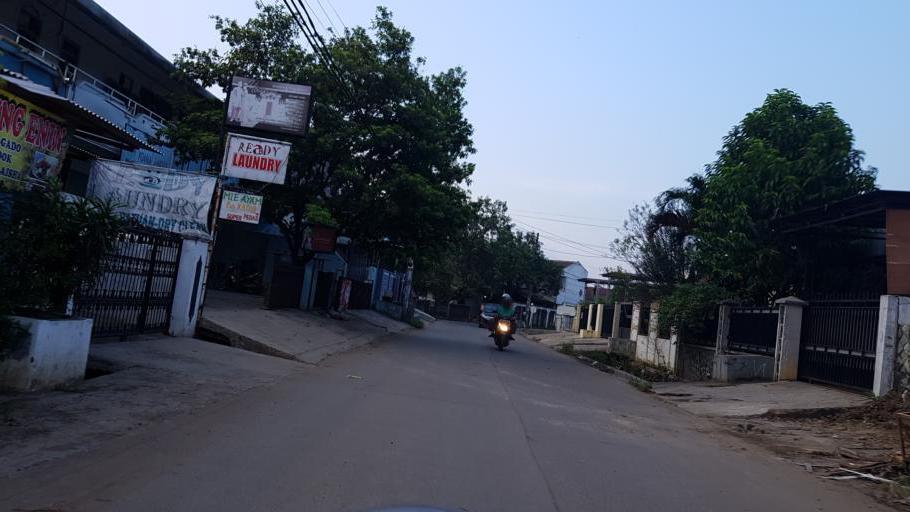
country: ID
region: West Java
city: Bekasi
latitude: -6.2711
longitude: 106.9468
